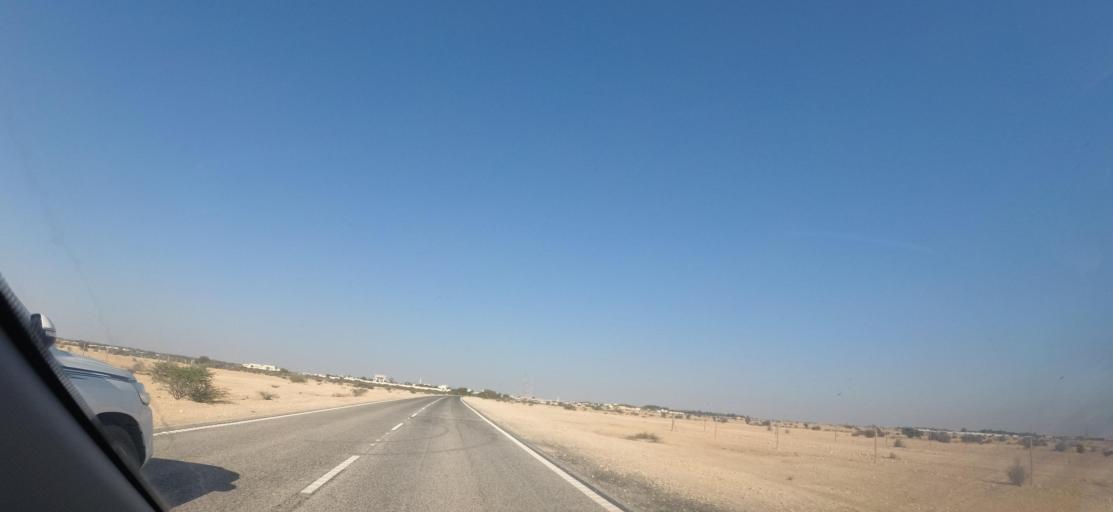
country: QA
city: Al Ghuwayriyah
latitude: 25.8199
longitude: 51.2368
